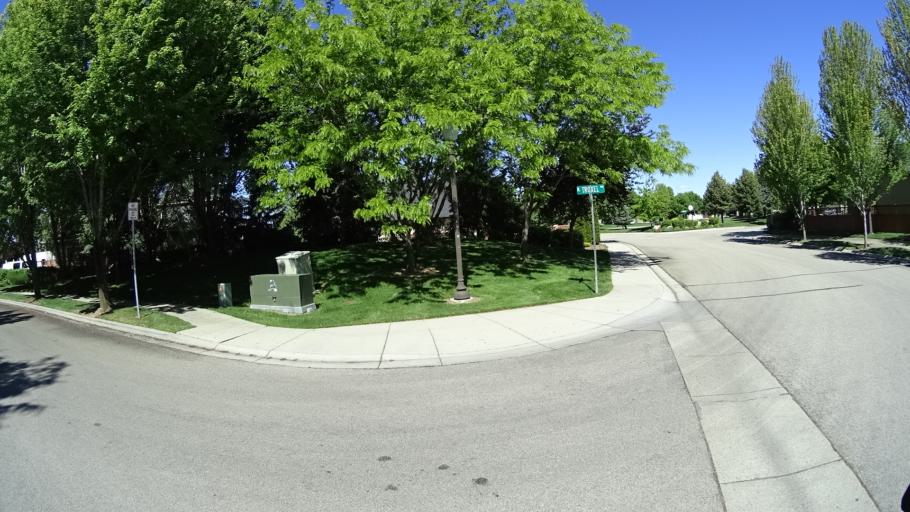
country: US
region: Idaho
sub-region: Ada County
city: Meridian
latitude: 43.6375
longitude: -116.3642
